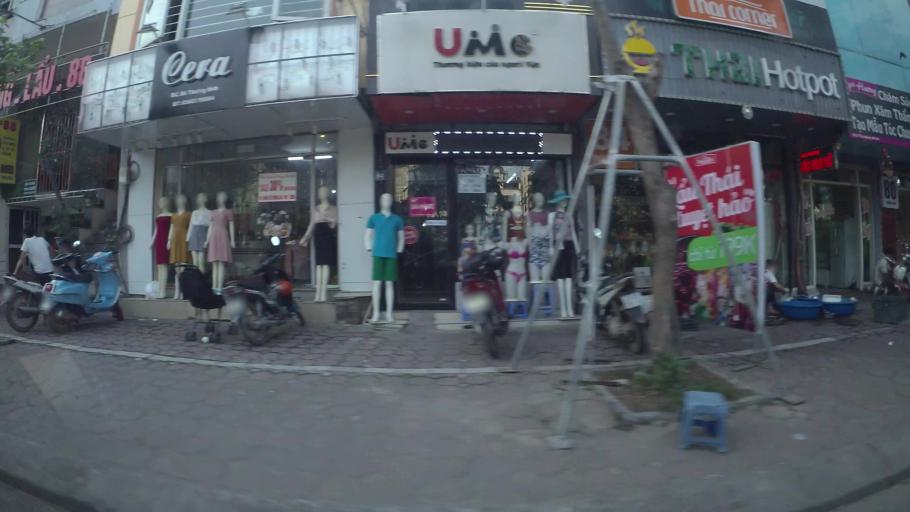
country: VN
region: Ha Noi
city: Thanh Xuan
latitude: 20.9994
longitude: 105.8175
